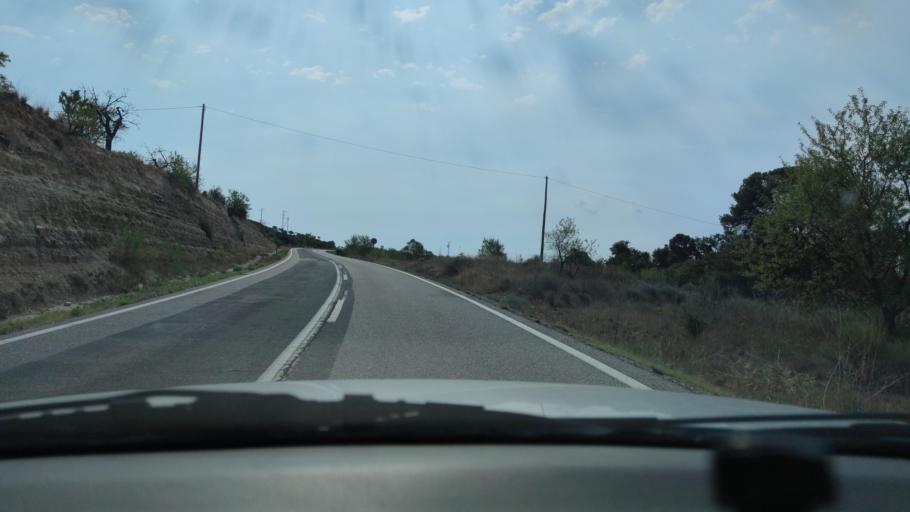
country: ES
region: Catalonia
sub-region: Provincia de Lleida
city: Arbeca
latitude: 41.5067
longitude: 0.9243
